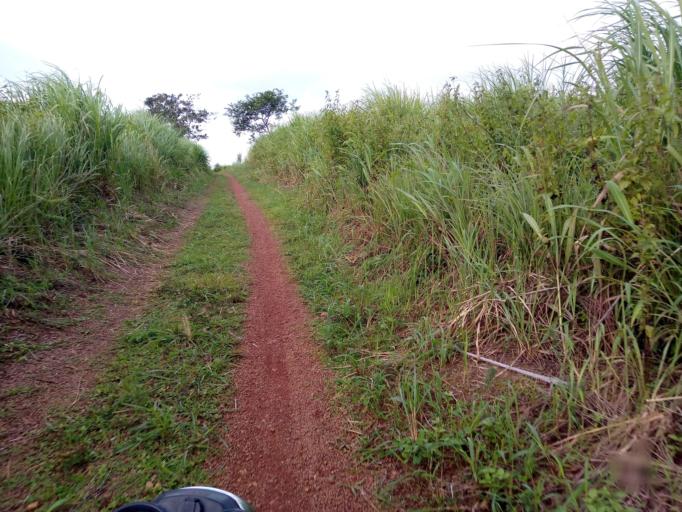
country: GN
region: Nzerekore
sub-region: Prefecture de Guekedou
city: Gueckedou
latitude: 8.4840
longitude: -10.3202
